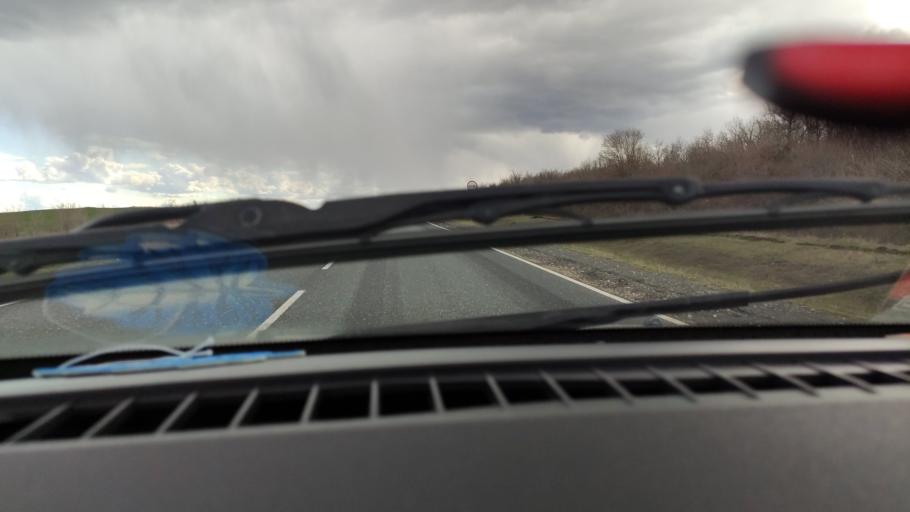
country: RU
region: Saratov
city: Balakovo
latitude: 52.1913
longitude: 47.8537
